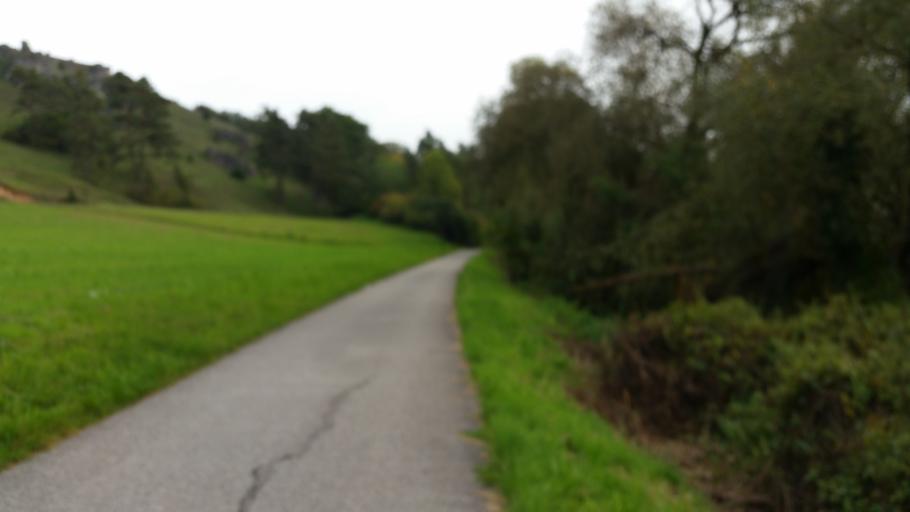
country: DE
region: Bavaria
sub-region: Upper Bavaria
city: Walting
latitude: 48.9336
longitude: 11.3360
